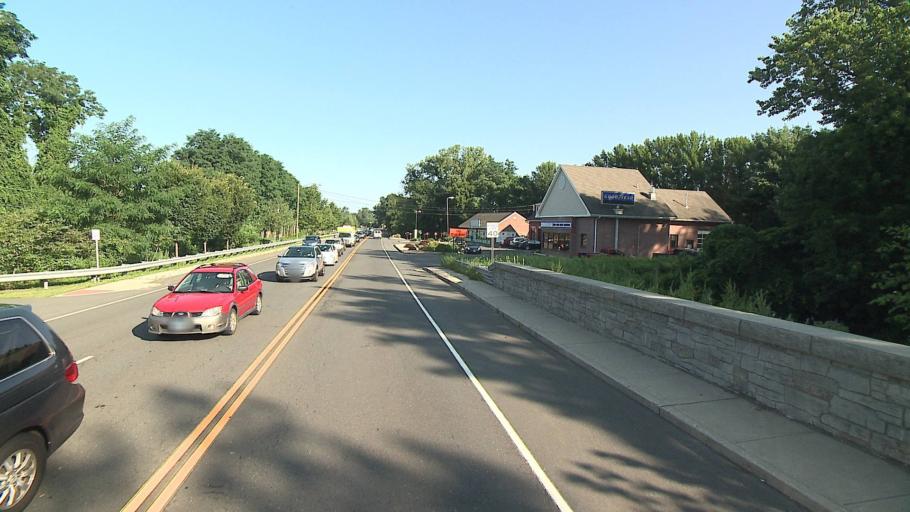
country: US
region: Connecticut
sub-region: Hartford County
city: Farmington
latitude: 41.7294
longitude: -72.8292
